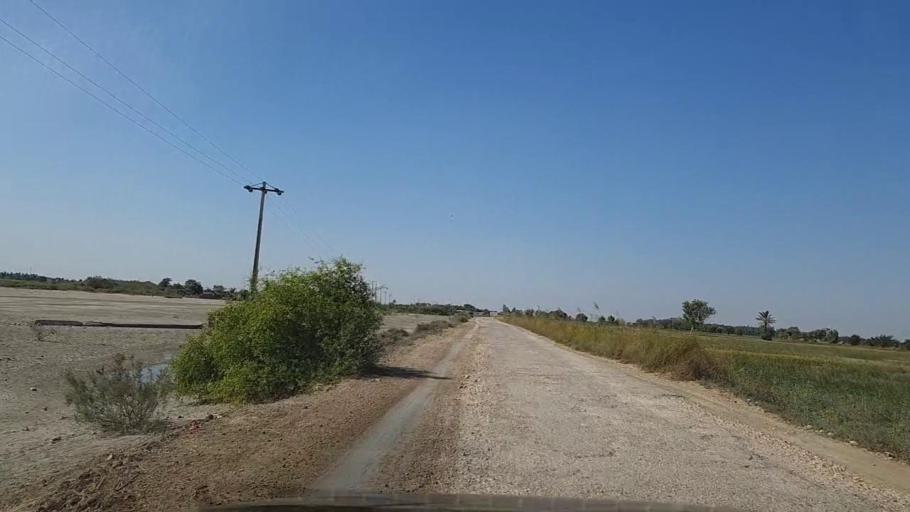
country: PK
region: Sindh
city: Mirpur Sakro
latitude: 24.6090
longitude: 67.7844
